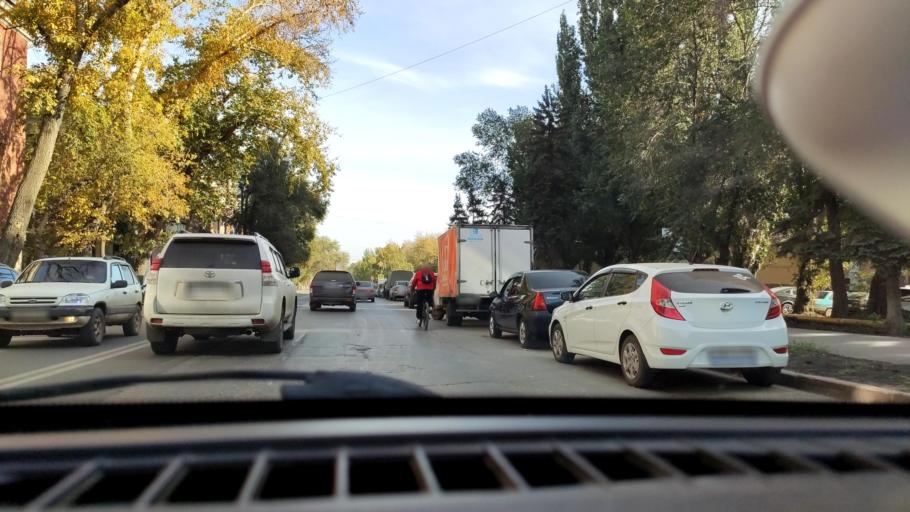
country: RU
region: Samara
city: Samara
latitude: 53.2162
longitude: 50.2604
